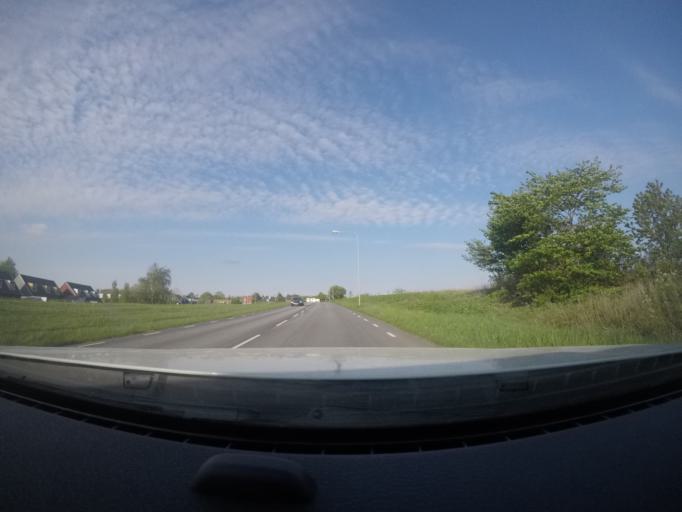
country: SE
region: Skane
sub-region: Helsingborg
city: Glumslov
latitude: 55.9360
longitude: 12.8130
